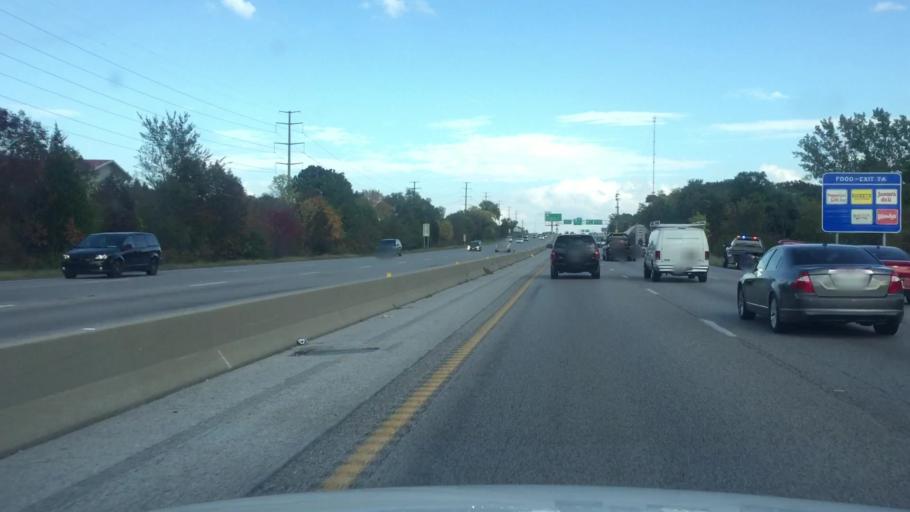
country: US
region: Missouri
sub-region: Jackson County
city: Lees Summit
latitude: 38.9350
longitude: -94.4305
